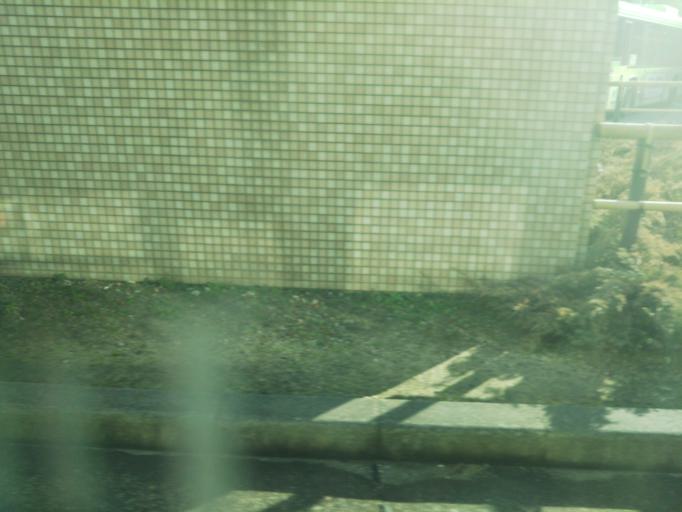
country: JP
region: Kyoto
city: Kyoto
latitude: 34.9873
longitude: 135.7578
